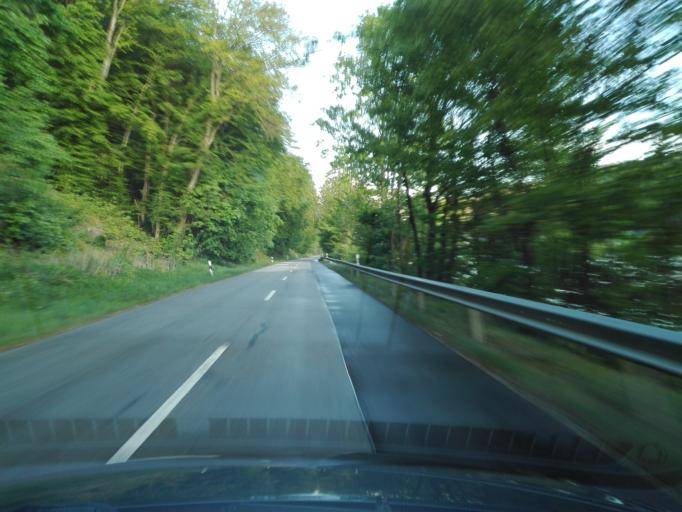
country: DE
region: Bavaria
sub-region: Lower Bavaria
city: Untergriesbach
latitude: 48.5267
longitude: 13.6927
